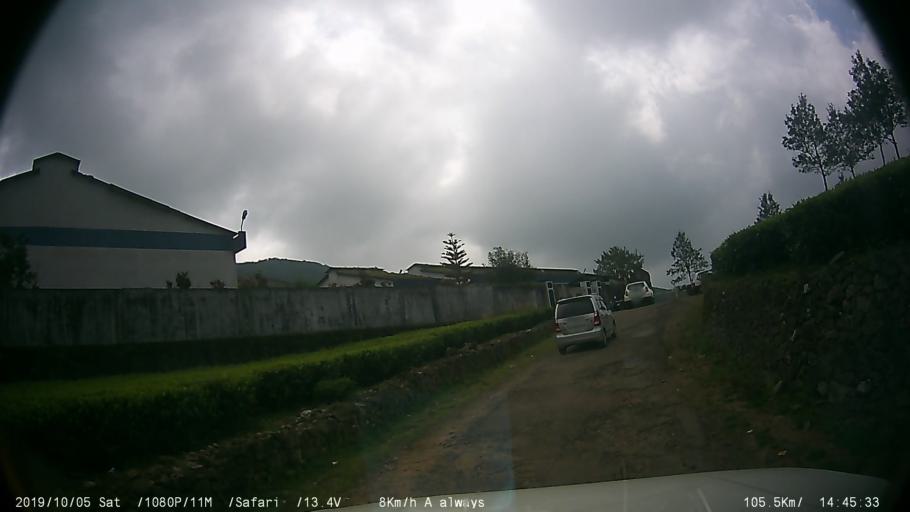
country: IN
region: Kerala
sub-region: Kottayam
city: Erattupetta
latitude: 9.6176
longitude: 76.9447
